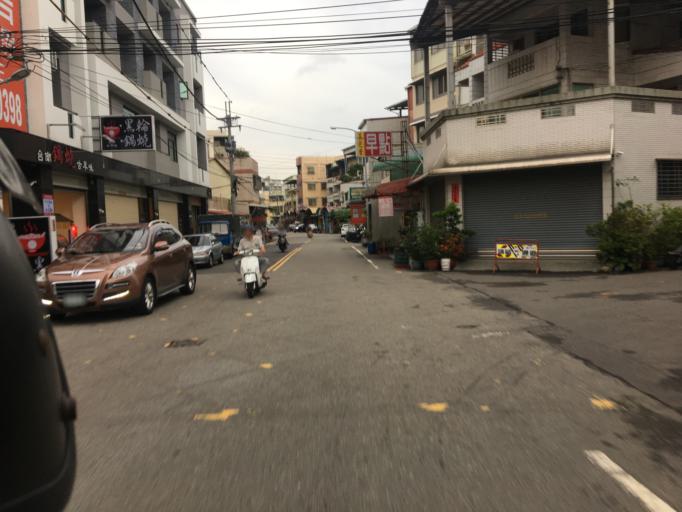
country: TW
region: Taiwan
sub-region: Taichung City
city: Taichung
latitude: 24.0904
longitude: 120.6995
